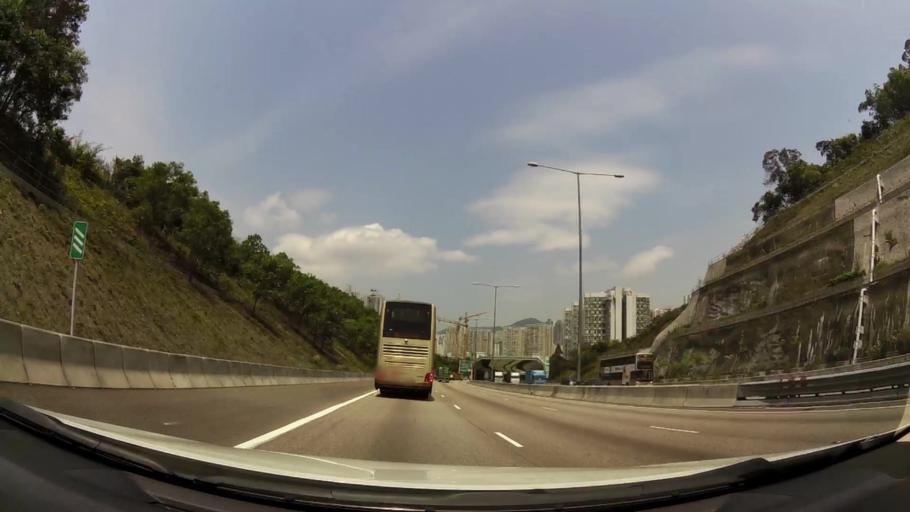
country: HK
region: Tuen Mun
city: Tuen Mun
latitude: 22.3816
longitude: 113.9821
